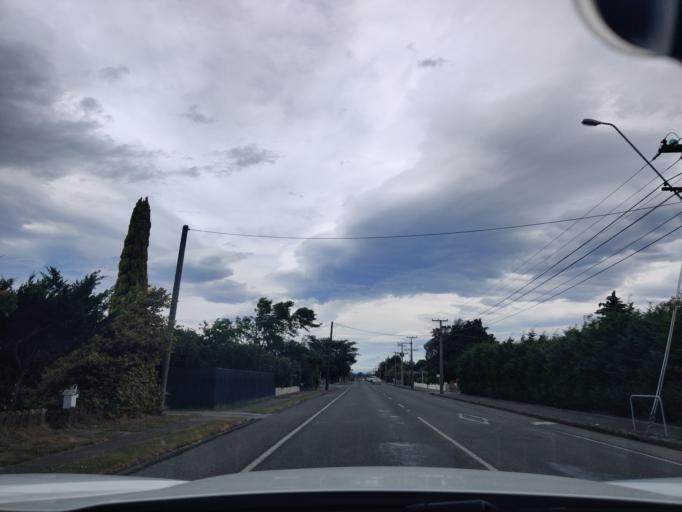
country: NZ
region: Wellington
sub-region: Masterton District
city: Masterton
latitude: -41.0401
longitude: 175.5120
